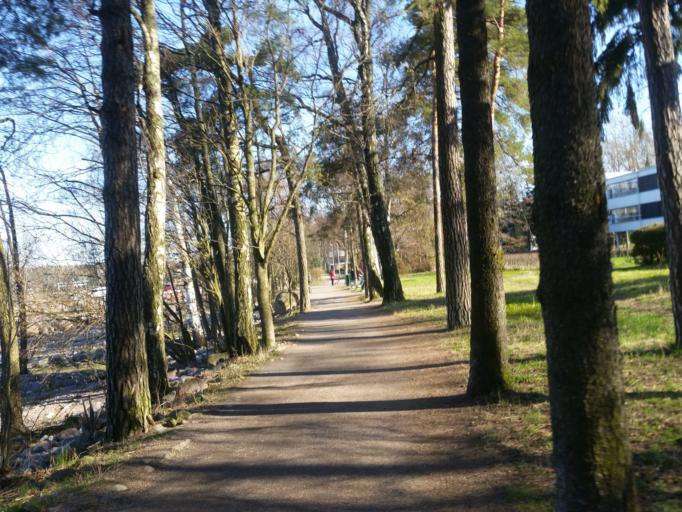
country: FI
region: Uusimaa
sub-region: Helsinki
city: Teekkarikylae
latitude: 60.1490
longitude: 24.8763
